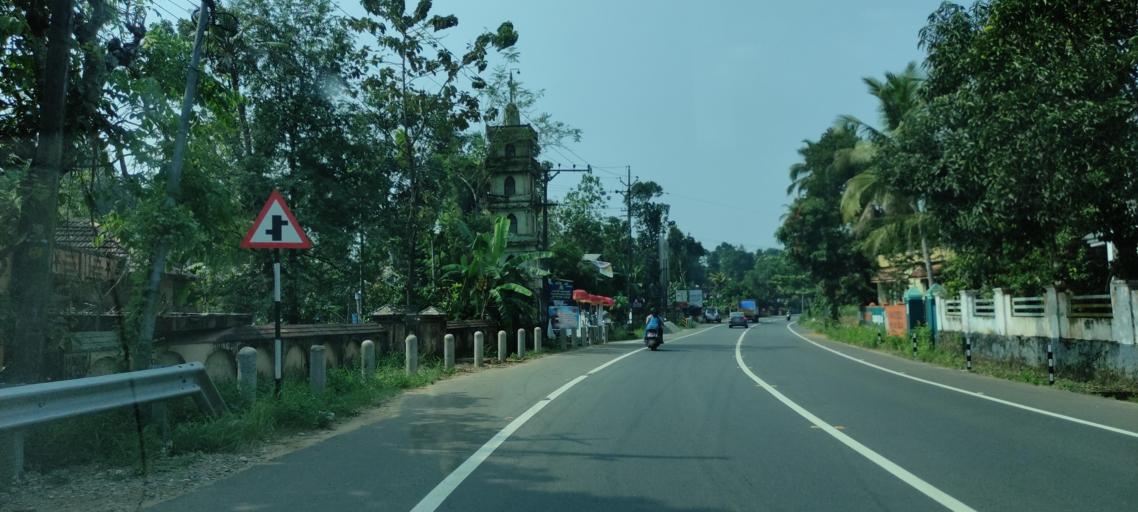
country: IN
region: Kerala
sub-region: Alappuzha
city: Chengannur
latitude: 9.2499
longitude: 76.6658
